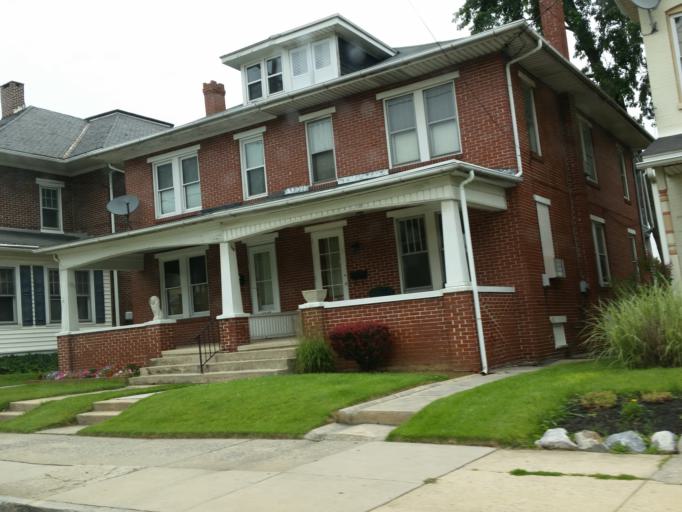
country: US
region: Pennsylvania
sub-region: York County
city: North York
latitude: 39.9796
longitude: -76.7336
